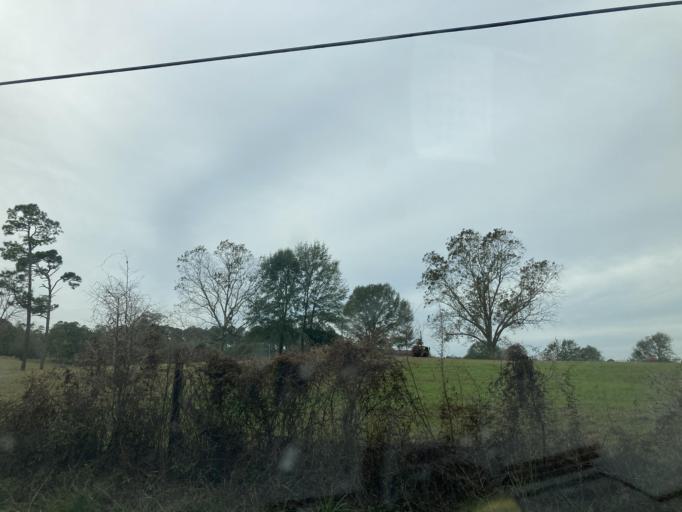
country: US
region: Mississippi
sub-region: Lamar County
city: Lumberton
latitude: 31.0401
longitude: -89.4165
